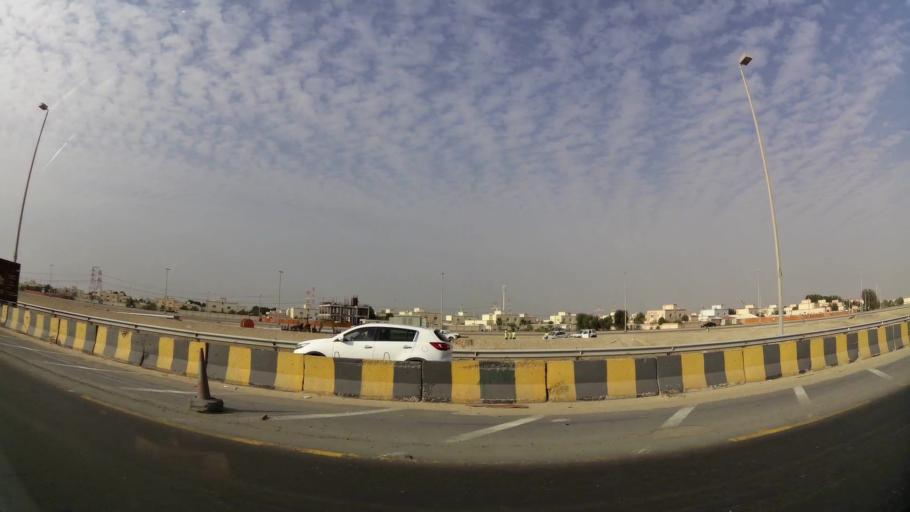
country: AE
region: Abu Dhabi
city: Abu Dhabi
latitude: 24.2930
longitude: 54.5538
